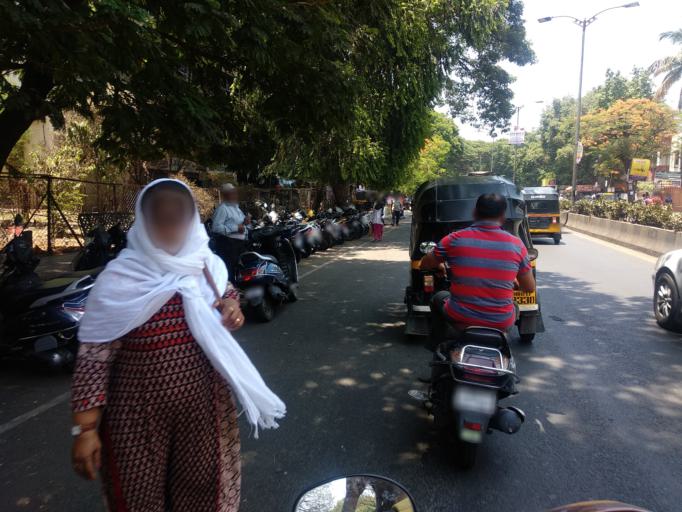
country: IN
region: Maharashtra
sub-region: Pune Division
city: Pune
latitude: 18.5074
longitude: 73.8442
